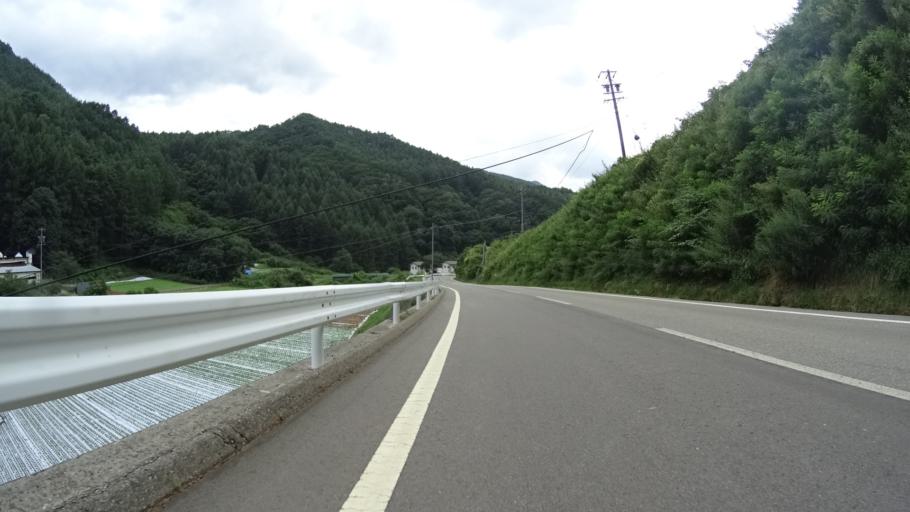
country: JP
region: Nagano
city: Saku
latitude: 36.0685
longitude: 138.5920
